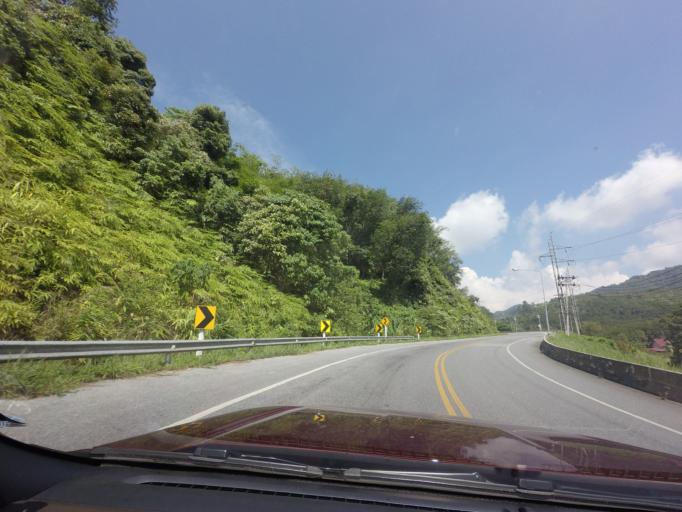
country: TH
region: Yala
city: Betong
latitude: 5.8582
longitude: 101.1239
